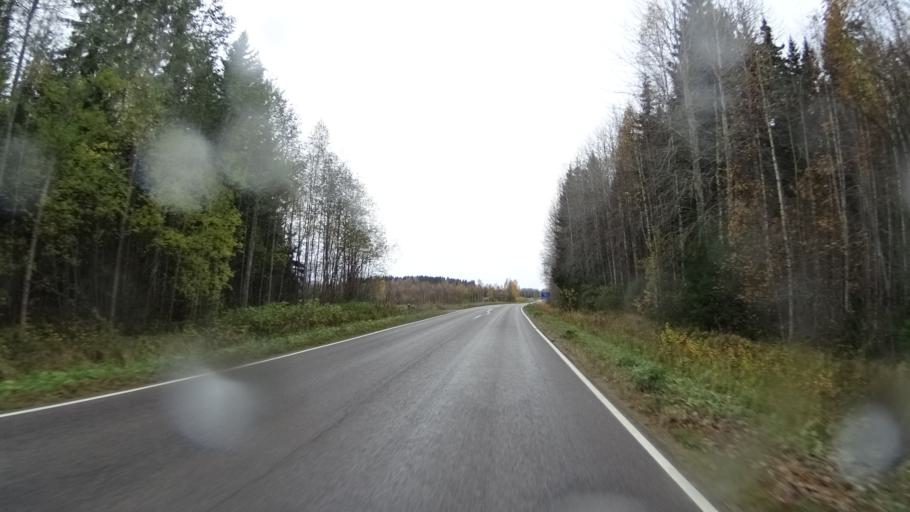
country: FI
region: Kymenlaakso
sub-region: Kouvola
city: Anjala
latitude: 60.6962
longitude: 26.8794
